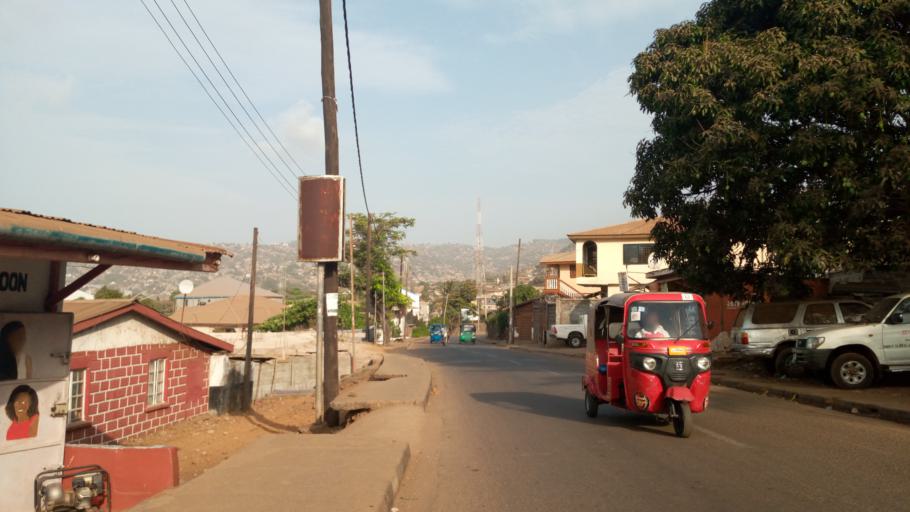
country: SL
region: Western Area
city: Freetown
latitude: 8.4743
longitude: -13.2532
